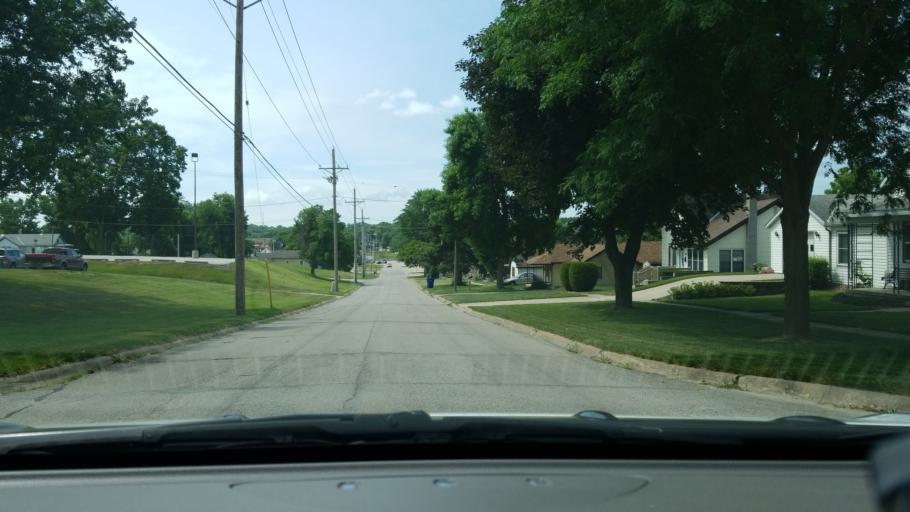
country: US
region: Nebraska
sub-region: Sarpy County
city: Papillion
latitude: 41.1604
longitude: -96.0442
